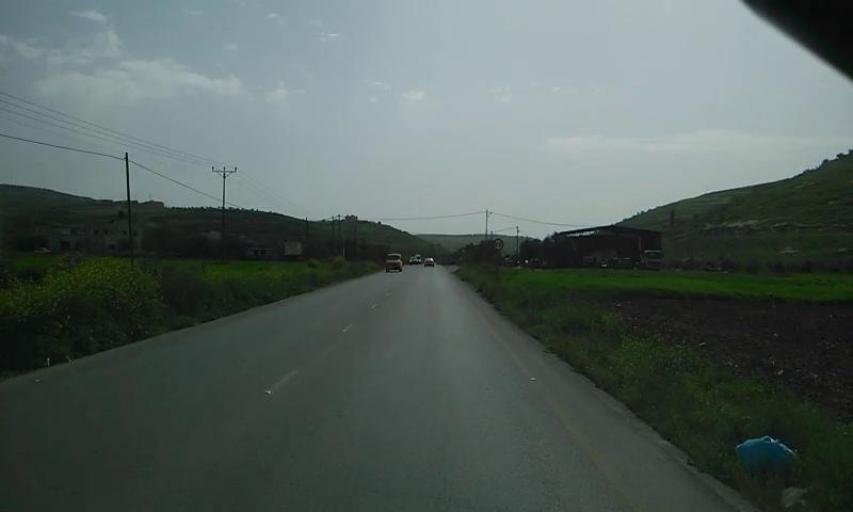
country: PS
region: West Bank
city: Mirkah
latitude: 32.3945
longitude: 35.2207
